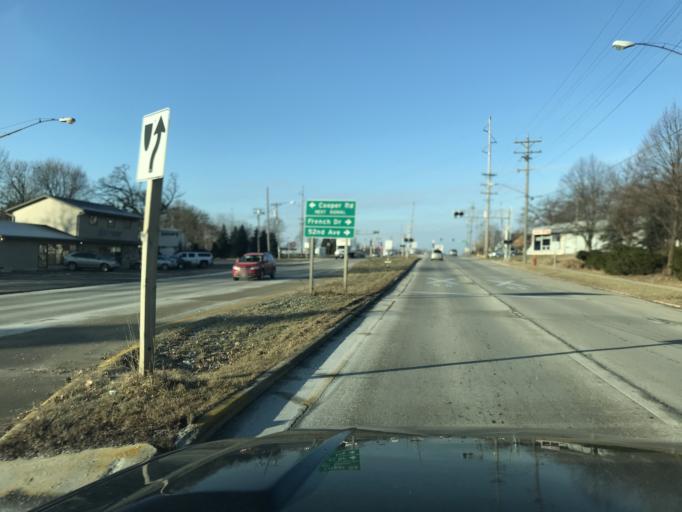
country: US
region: Wisconsin
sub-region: Kenosha County
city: Kenosha
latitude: 42.5663
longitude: -87.8671
